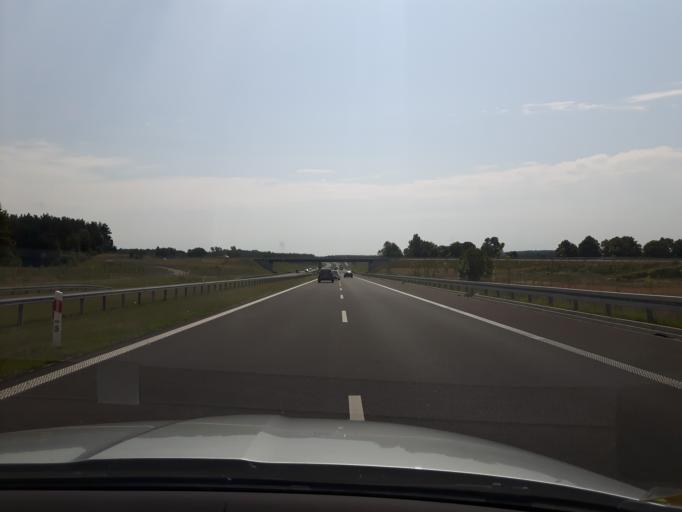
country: PL
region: Warmian-Masurian Voivodeship
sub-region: Powiat nidzicki
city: Nidzica
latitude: 53.3151
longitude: 20.4380
